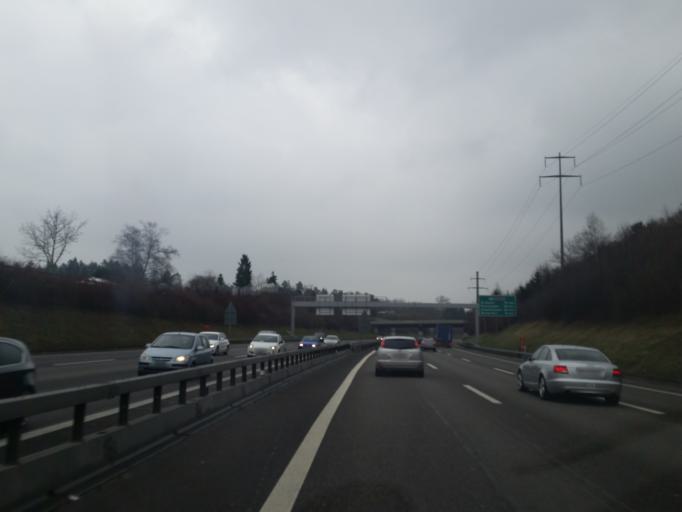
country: CH
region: Zurich
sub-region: Bezirk Uster
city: Bruttisellen
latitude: 47.4202
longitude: 8.6336
